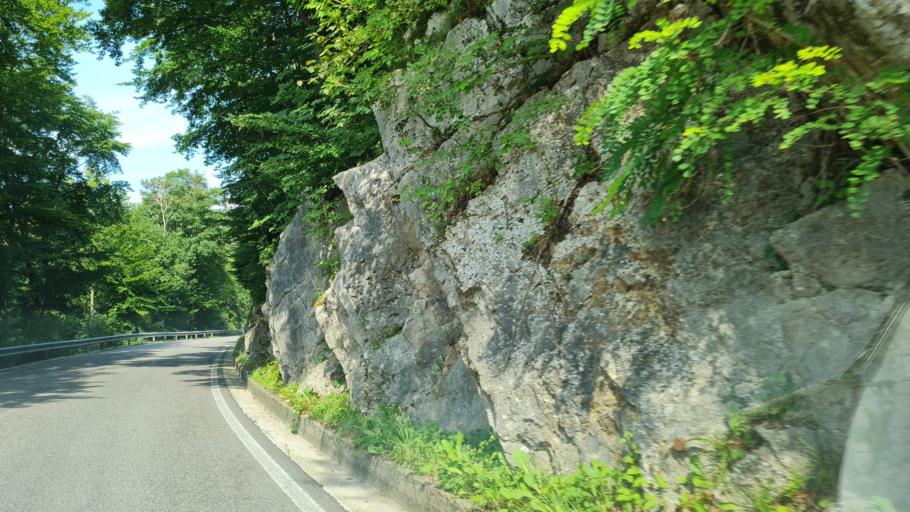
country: IT
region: Veneto
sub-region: Provincia di Vicenza
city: Conco
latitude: 45.7894
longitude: 11.6287
